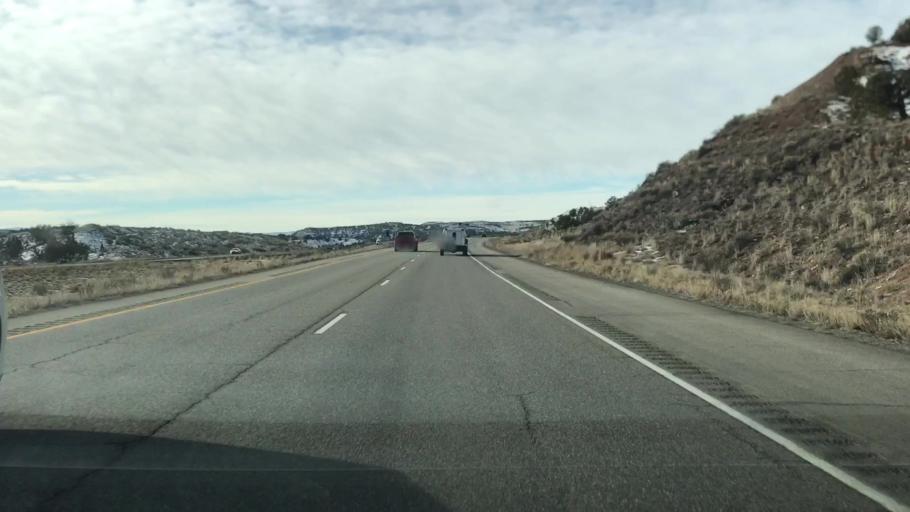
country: US
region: Colorado
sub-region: Garfield County
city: Parachute
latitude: 39.3800
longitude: -108.1562
